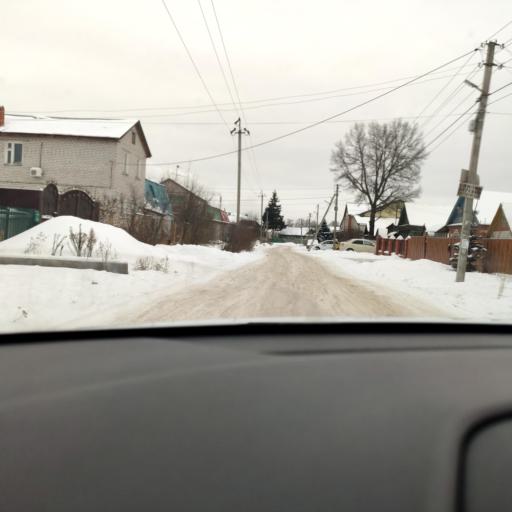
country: RU
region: Tatarstan
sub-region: Gorod Kazan'
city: Kazan
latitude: 55.8647
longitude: 49.0573
